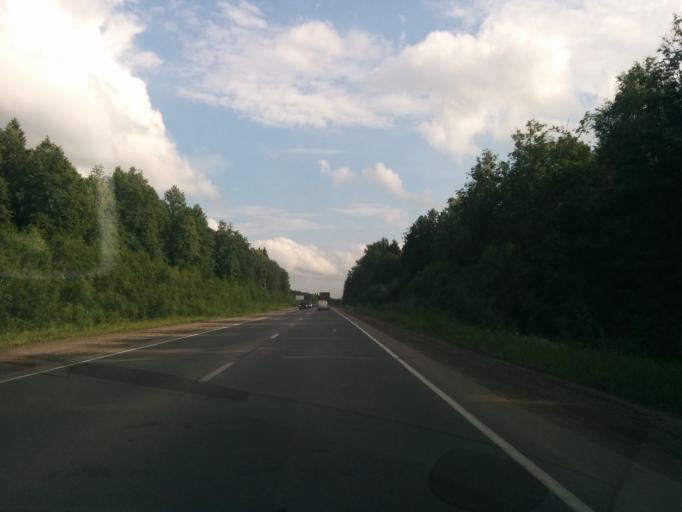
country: RU
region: Perm
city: Polazna
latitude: 58.1213
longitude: 56.4244
